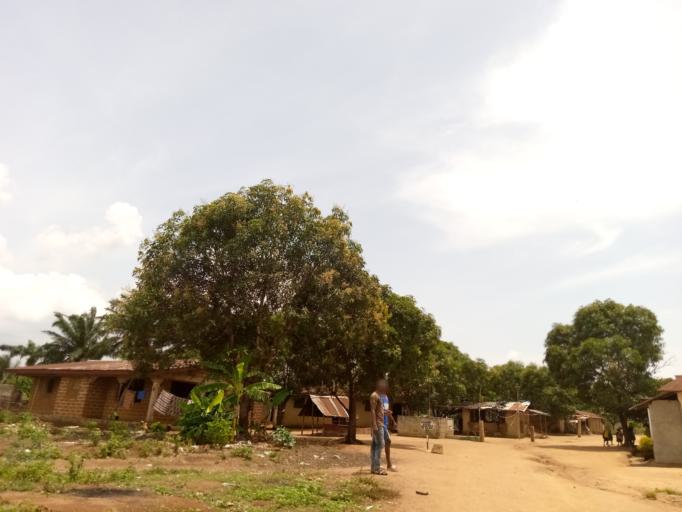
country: SL
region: Western Area
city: Waterloo
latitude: 8.3296
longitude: -13.0425
